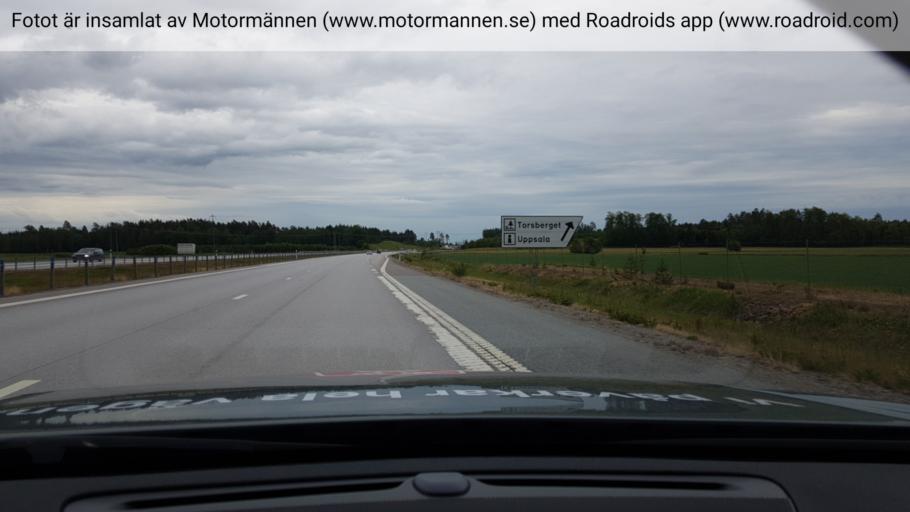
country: SE
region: Uppsala
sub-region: Uppsala Kommun
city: Storvreta
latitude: 59.9760
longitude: 17.6437
